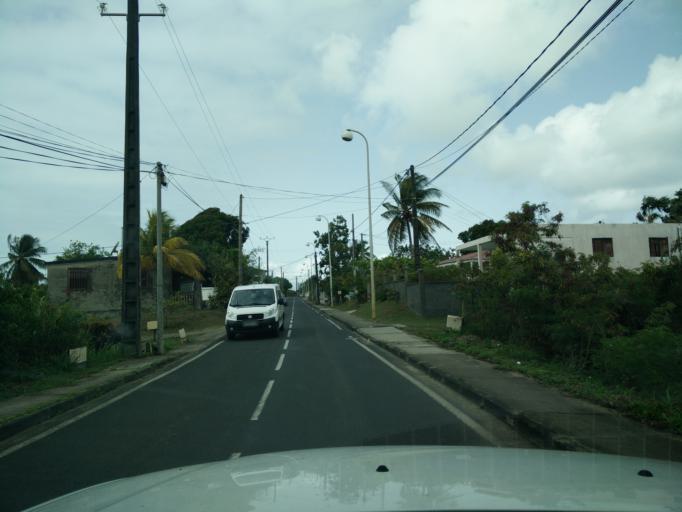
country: GP
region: Guadeloupe
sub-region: Guadeloupe
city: Le Gosier
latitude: 16.2189
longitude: -61.4581
